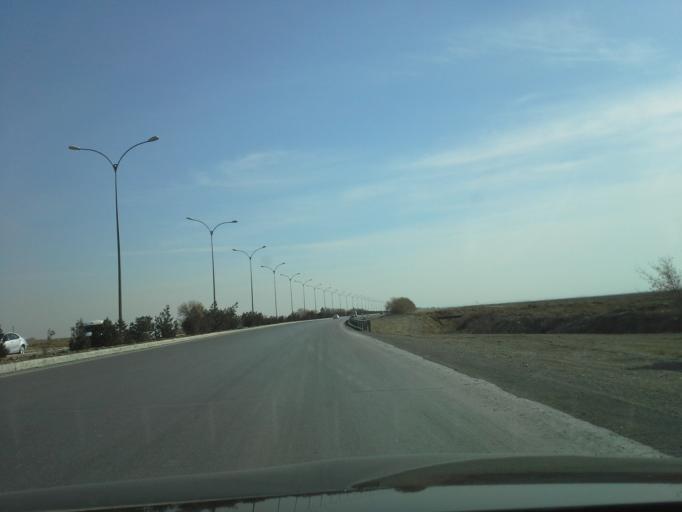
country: TM
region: Ahal
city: Abadan
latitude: 38.1342
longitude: 58.0152
